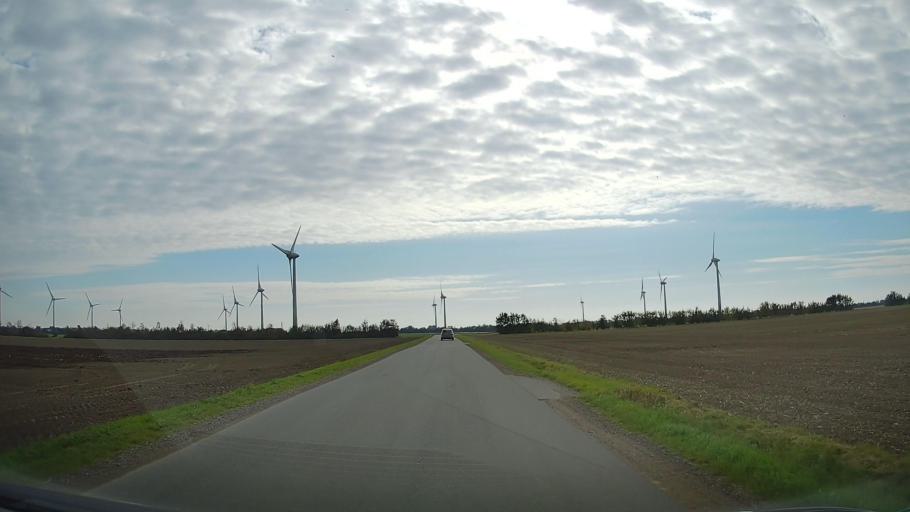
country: DE
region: Schleswig-Holstein
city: Grossenbrode
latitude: 54.5187
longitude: 11.0548
